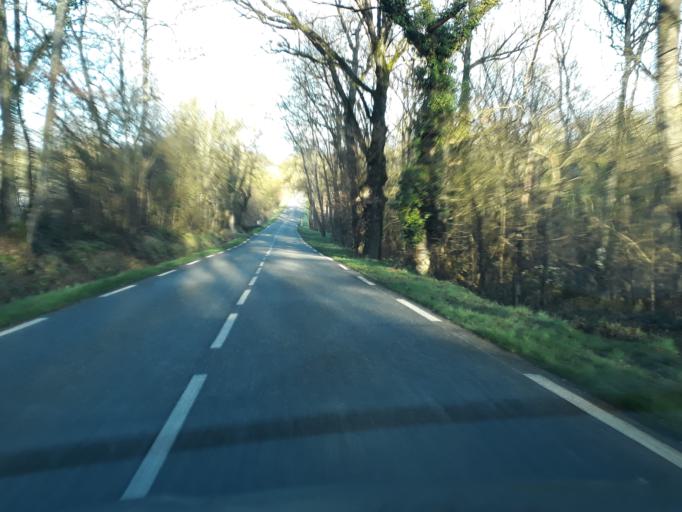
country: FR
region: Midi-Pyrenees
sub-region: Departement du Gers
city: Pujaudran
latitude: 43.5579
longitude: 1.1337
